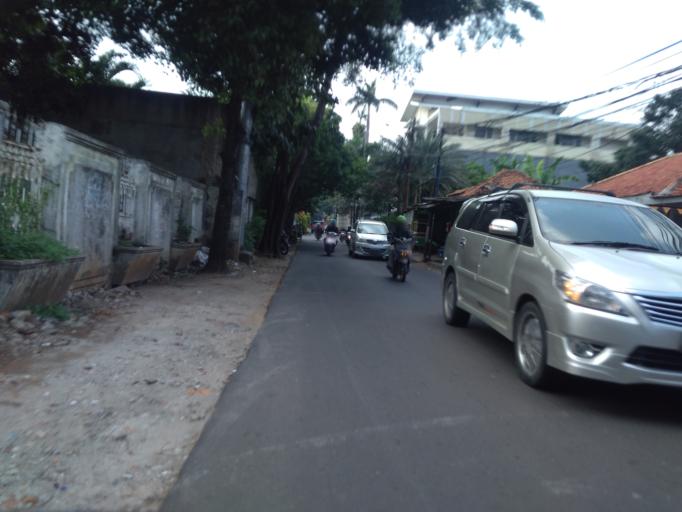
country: ID
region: Jakarta Raya
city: Jakarta
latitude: -6.2728
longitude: 106.8095
